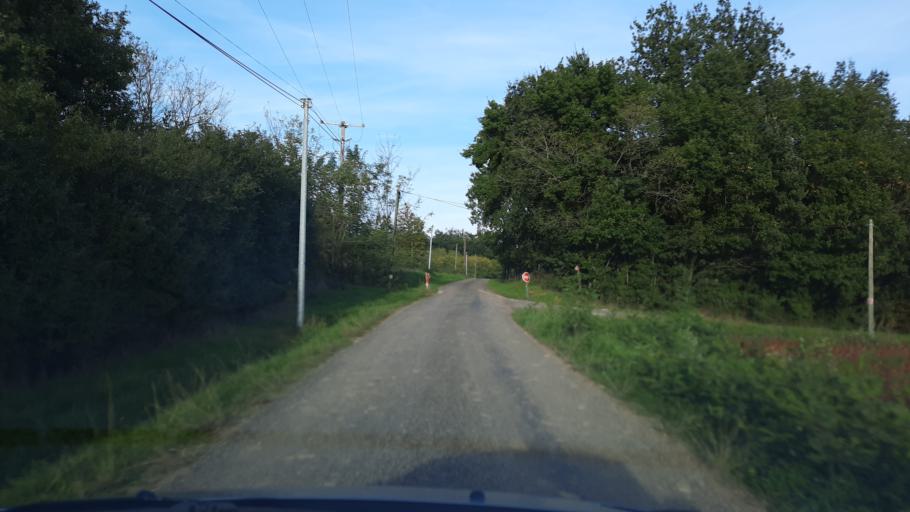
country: FR
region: Midi-Pyrenees
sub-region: Departement du Tarn-et-Garonne
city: Molieres
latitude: 44.1753
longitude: 1.3029
